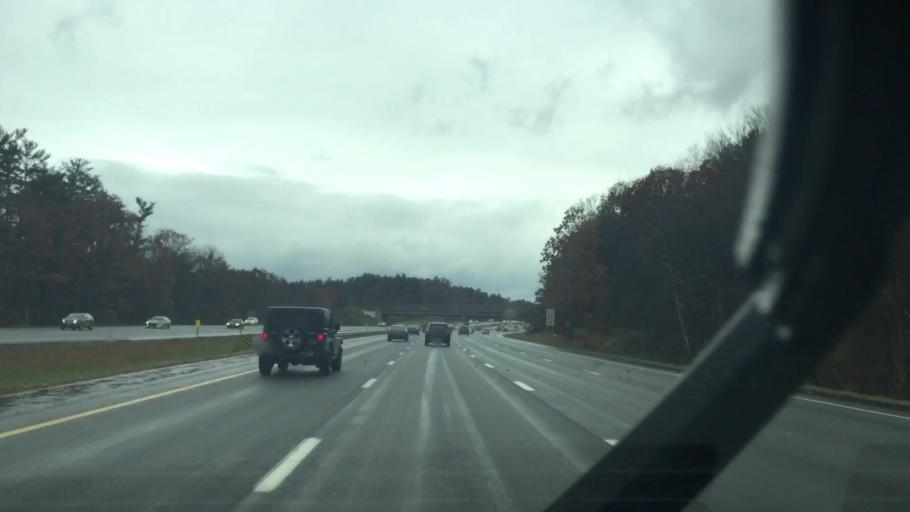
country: US
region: New Hampshire
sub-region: Rockingham County
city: Seabrook
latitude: 42.9032
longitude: -70.8778
